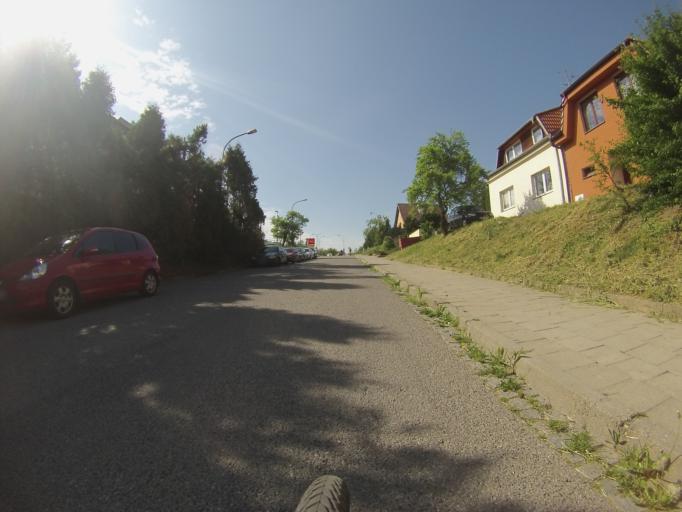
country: CZ
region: South Moravian
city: Troubsko
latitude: 49.2276
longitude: 16.5244
